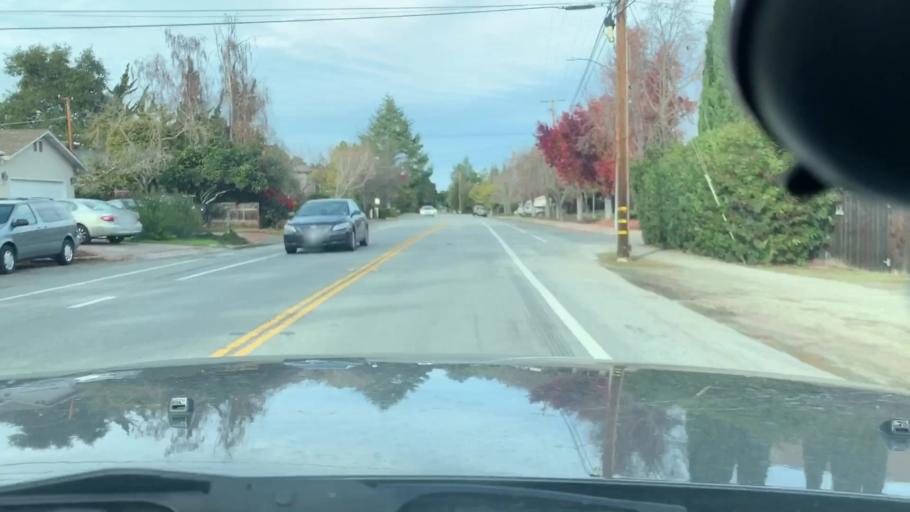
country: US
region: California
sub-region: Santa Clara County
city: Mountain View
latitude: 37.3795
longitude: -122.0960
